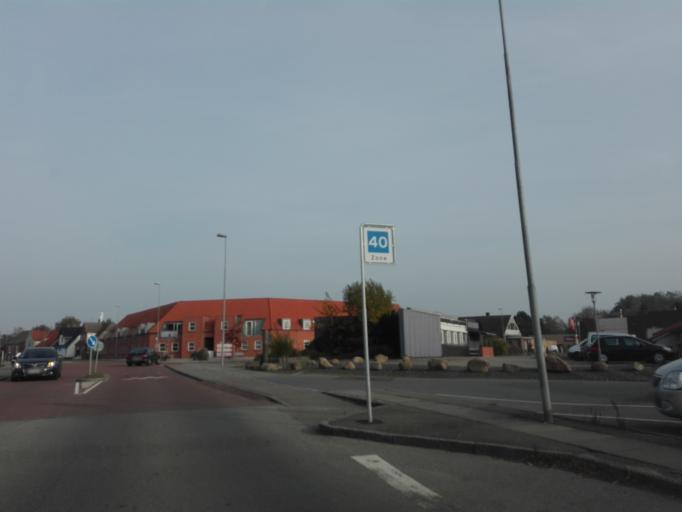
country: DK
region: Central Jutland
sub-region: Arhus Kommune
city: Solbjerg
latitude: 56.0374
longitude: 10.0809
